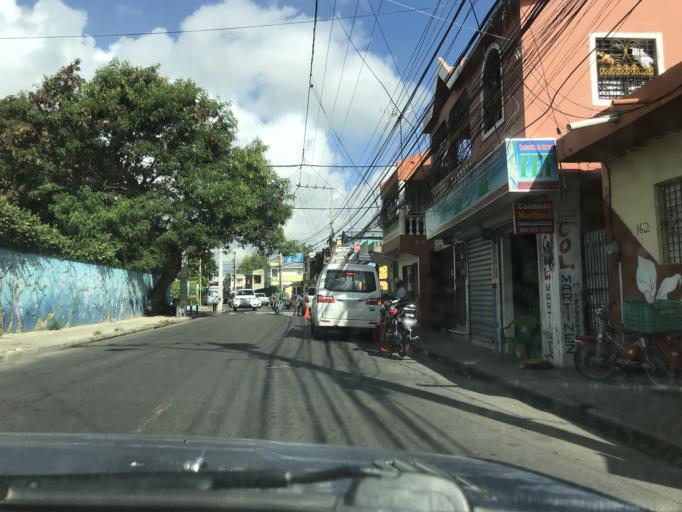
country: DO
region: Santiago
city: Santiago de los Caballeros
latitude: 19.4552
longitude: -70.7208
